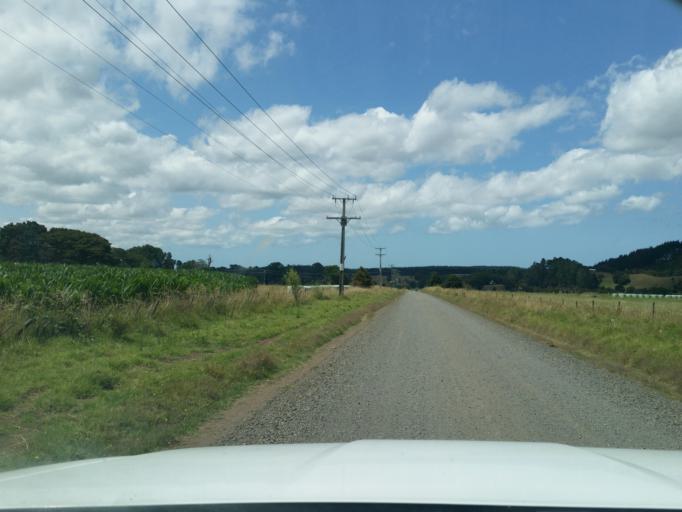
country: NZ
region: Northland
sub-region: Kaipara District
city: Dargaville
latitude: -35.7956
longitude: 173.7318
